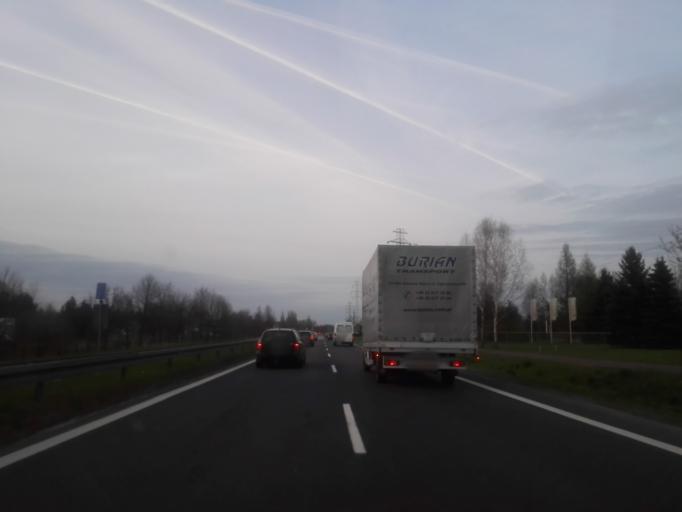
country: PL
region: Masovian Voivodeship
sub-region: Powiat pruszkowski
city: Nadarzyn
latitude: 52.0896
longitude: 20.8105
